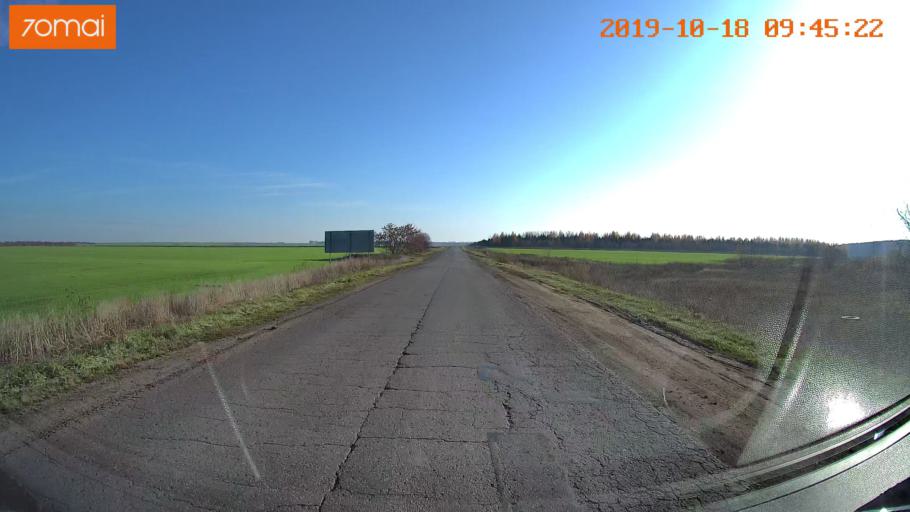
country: RU
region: Tula
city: Kazachka
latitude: 53.3125
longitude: 38.1880
